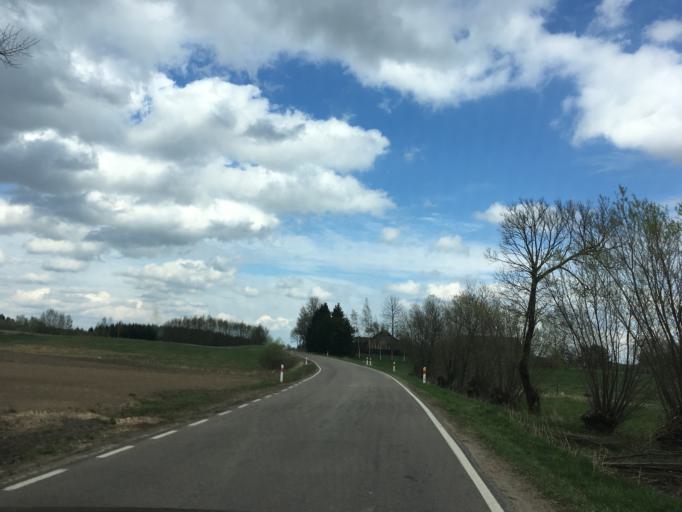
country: LT
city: Virbalis
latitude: 54.3640
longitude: 22.8444
